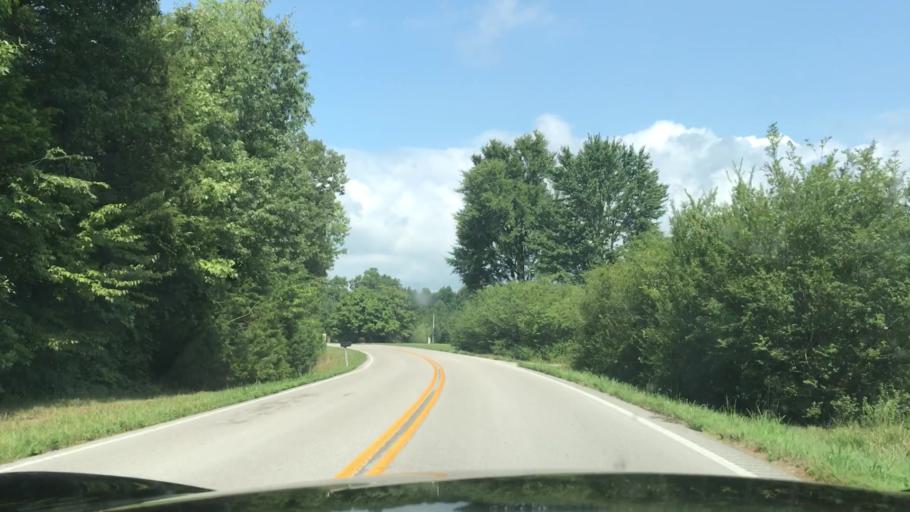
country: US
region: Kentucky
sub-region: Butler County
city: Morgantown
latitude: 37.1815
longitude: -86.8668
